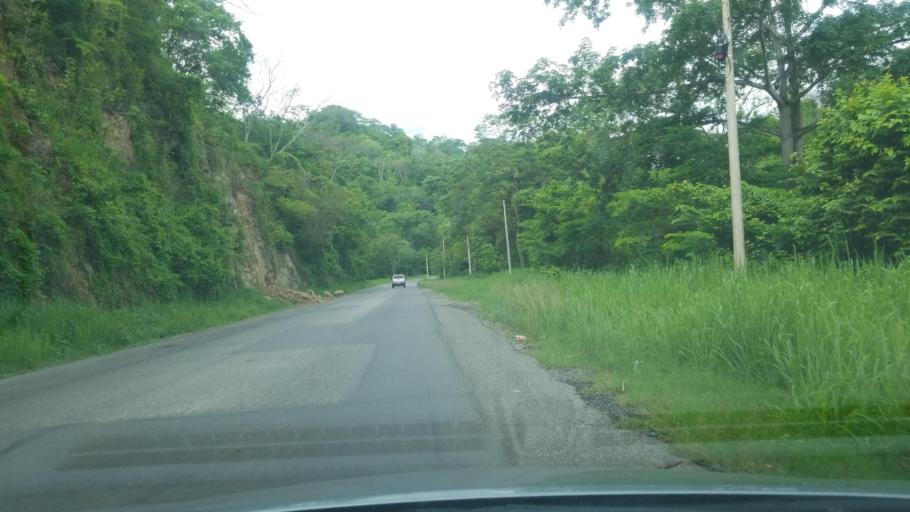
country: HN
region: Santa Barbara
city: Camalote
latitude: 15.3276
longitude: -88.3043
